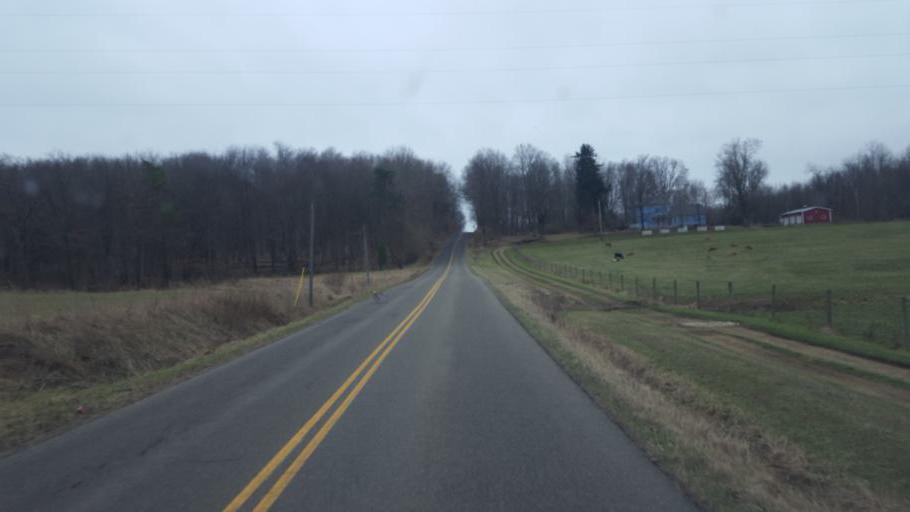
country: US
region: Ohio
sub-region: Knox County
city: Fredericktown
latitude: 40.4711
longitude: -82.4837
